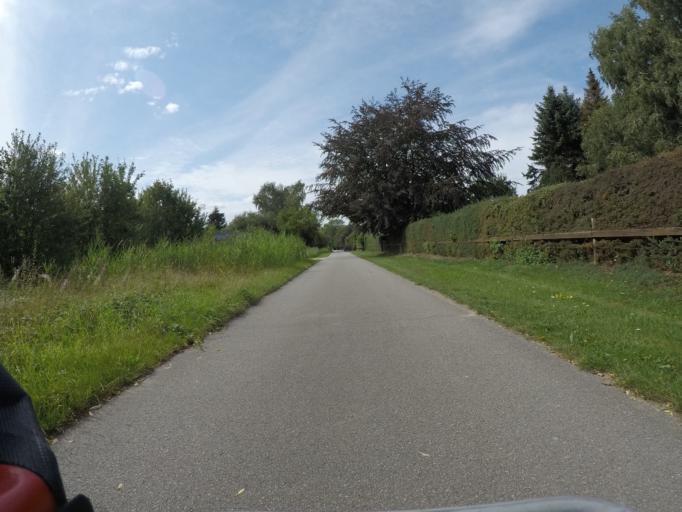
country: DE
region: Lower Saxony
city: Drage
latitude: 53.3699
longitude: 10.2711
